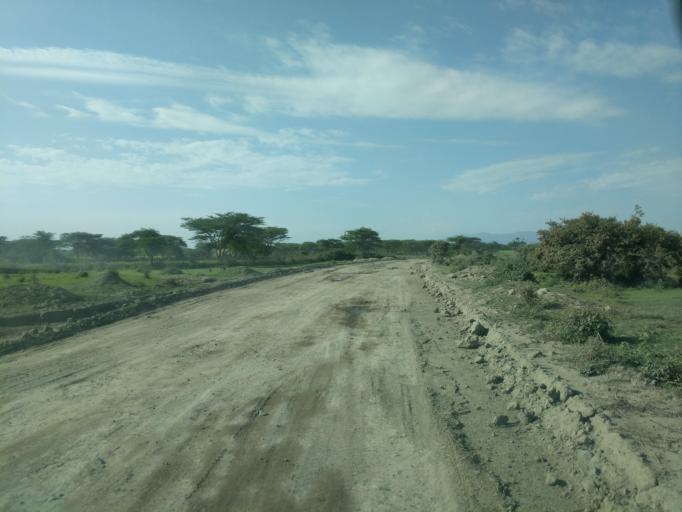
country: ET
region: Oromiya
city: Ziway
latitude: 7.5832
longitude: 38.6825
